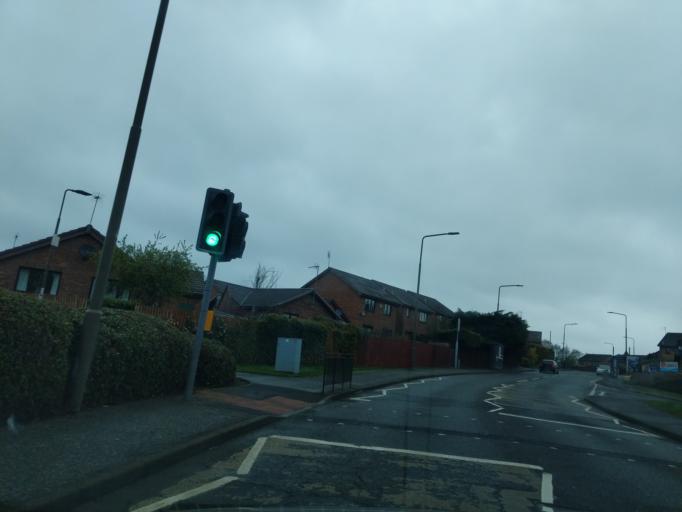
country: GB
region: Scotland
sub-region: East Lothian
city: Musselburgh
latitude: 55.9366
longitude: -3.0740
